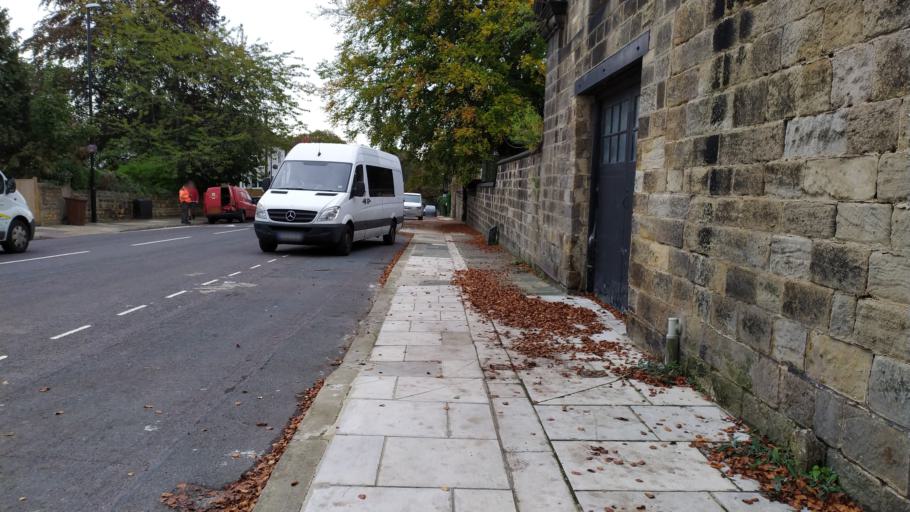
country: GB
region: England
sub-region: City and Borough of Leeds
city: Chapel Allerton
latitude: 53.8270
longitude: -1.5773
